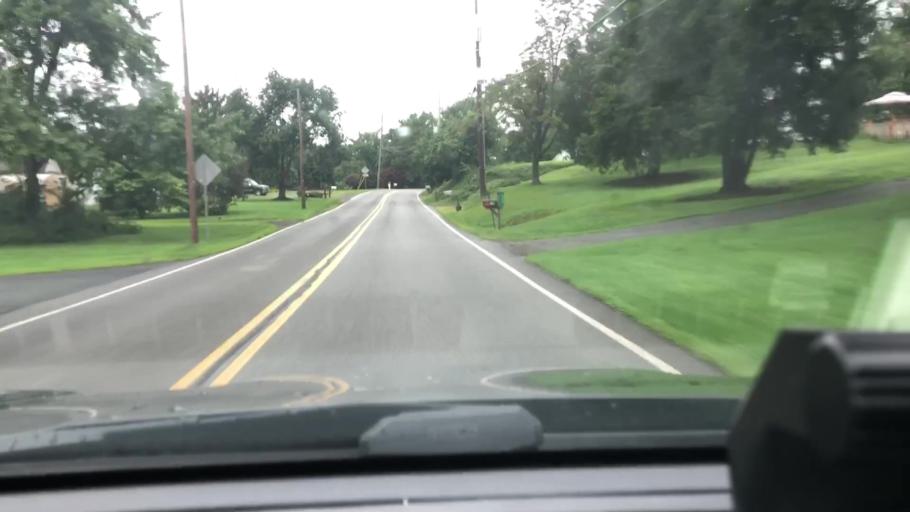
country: US
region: Pennsylvania
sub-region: Montgomery County
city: Gilbertsville
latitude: 40.3014
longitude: -75.6190
